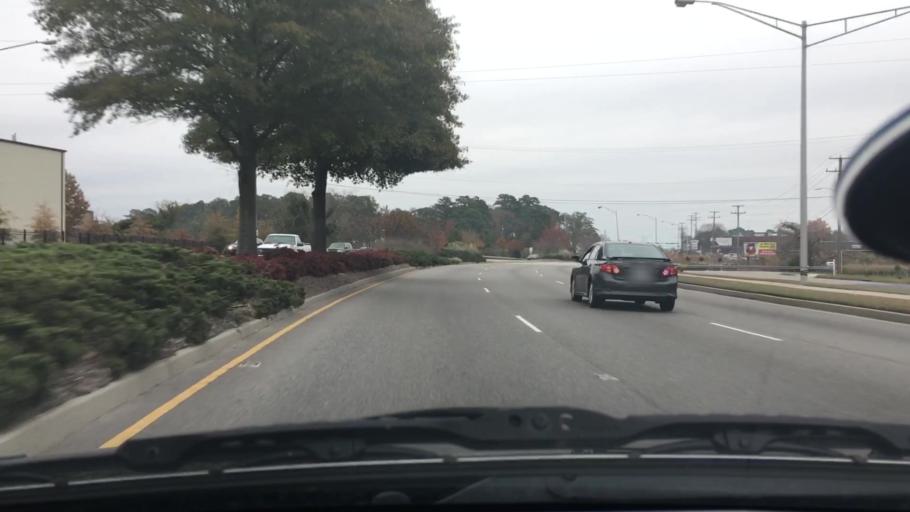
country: US
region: Virginia
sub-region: City of Norfolk
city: Norfolk
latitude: 36.8564
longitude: -76.2297
